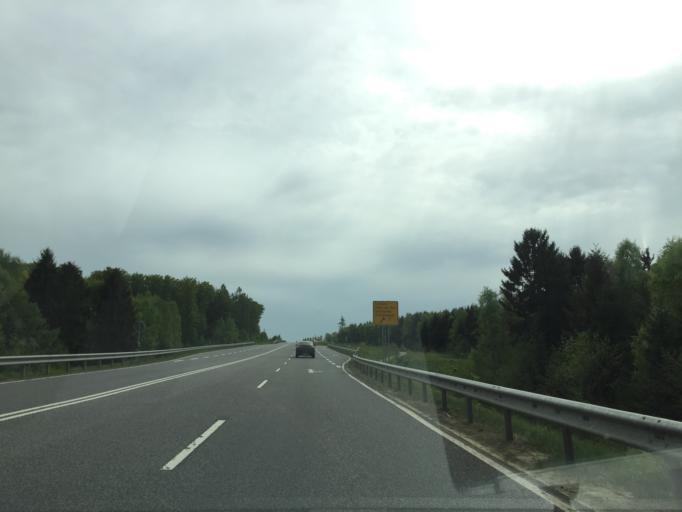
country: DE
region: Rheinland-Pfalz
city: Ettinghausen
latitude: 50.5251
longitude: 7.8805
